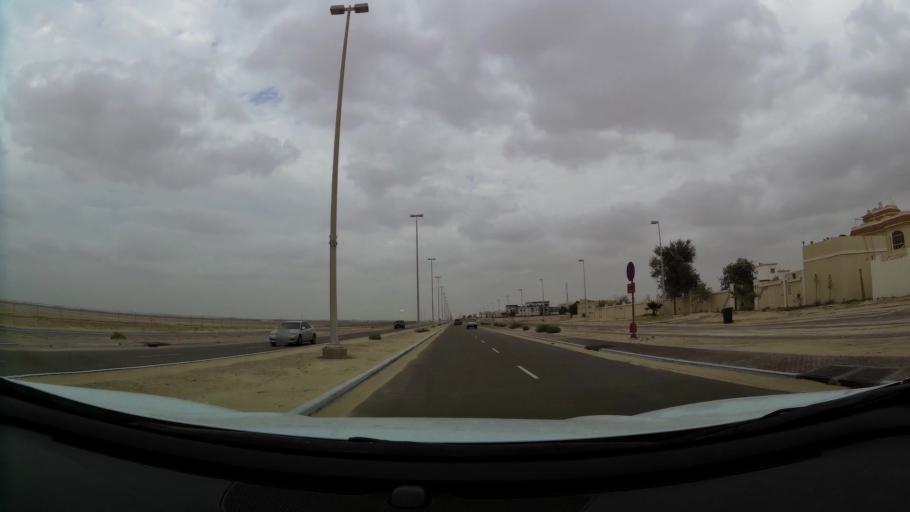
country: AE
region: Abu Dhabi
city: Abu Dhabi
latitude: 24.3798
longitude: 54.6325
